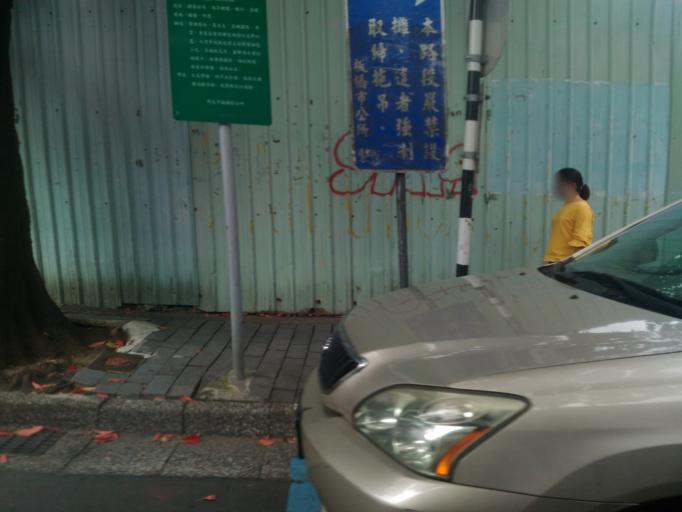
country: TW
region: Taipei
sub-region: Taipei
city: Banqiao
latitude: 25.0114
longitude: 121.4564
